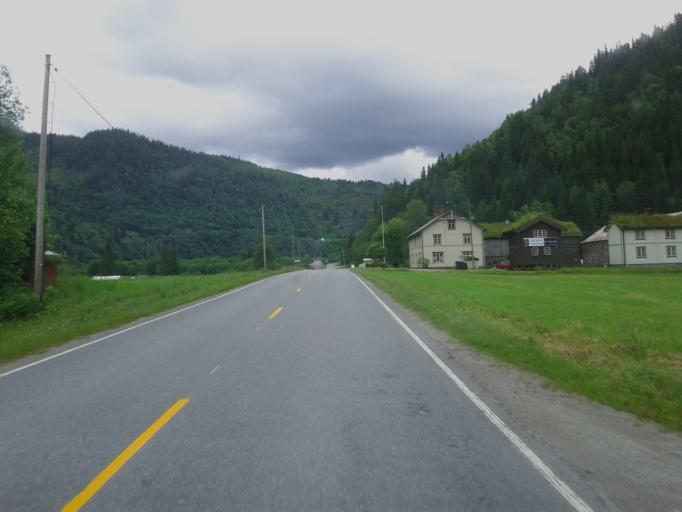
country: NO
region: Sor-Trondelag
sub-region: Midtre Gauldal
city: Storen
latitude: 62.9502
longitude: 10.6129
